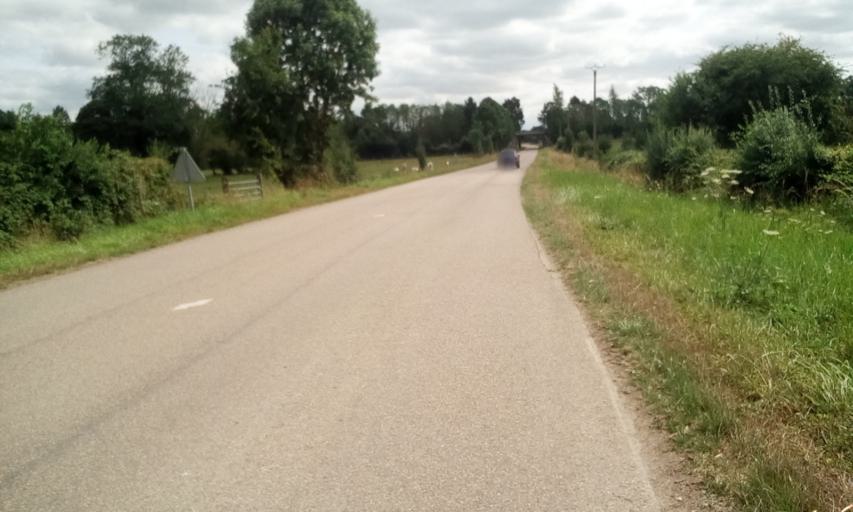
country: FR
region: Lower Normandy
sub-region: Departement du Calvados
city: Troarn
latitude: 49.2033
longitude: -0.1770
